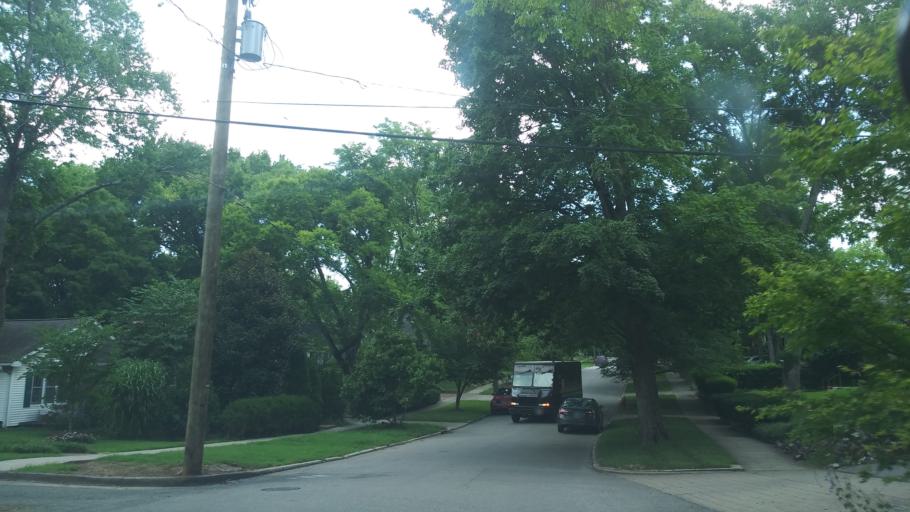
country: US
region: Tennessee
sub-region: Davidson County
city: Nashville
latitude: 36.1381
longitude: -86.8249
